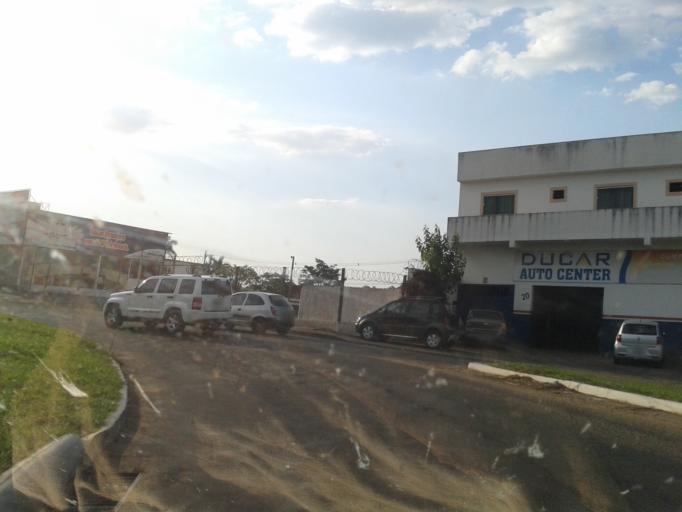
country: BR
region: Minas Gerais
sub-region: Uberlandia
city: Uberlandia
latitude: -18.9388
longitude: -48.3071
